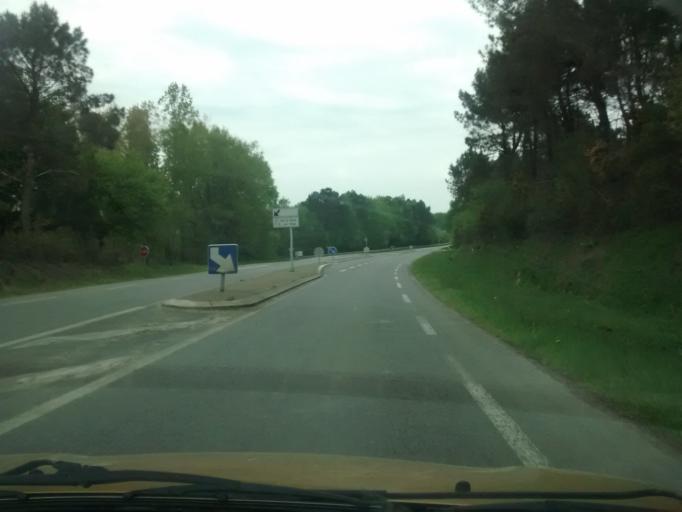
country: FR
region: Brittany
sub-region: Departement du Morbihan
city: Berric
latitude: 47.6010
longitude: -2.5486
